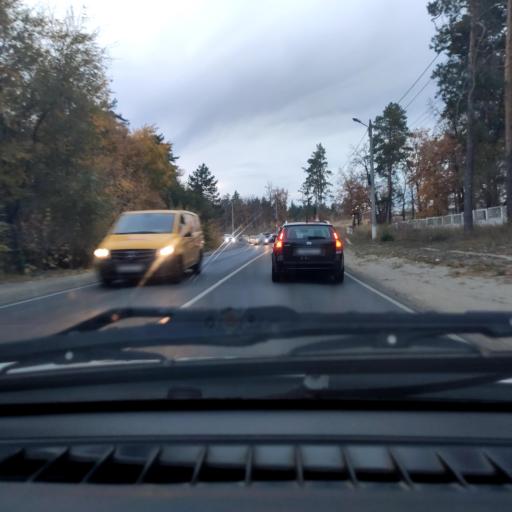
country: RU
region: Samara
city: Tol'yatti
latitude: 53.4851
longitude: 49.3153
